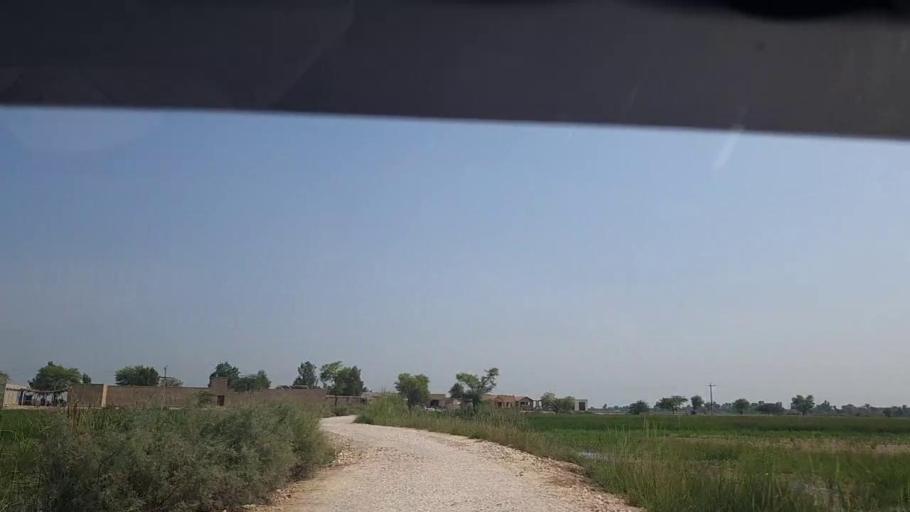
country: PK
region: Sindh
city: Thul
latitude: 28.1948
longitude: 68.7338
